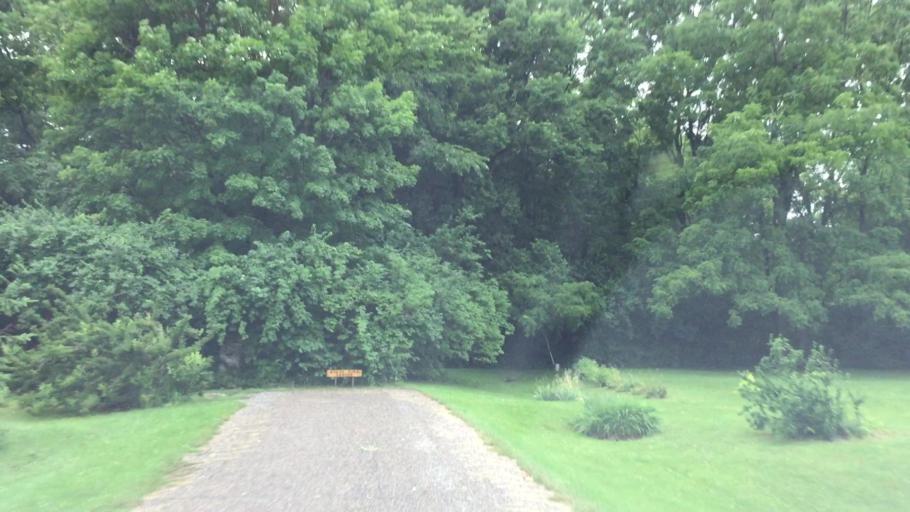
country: US
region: Illinois
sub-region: Hancock County
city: Nauvoo
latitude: 40.5326
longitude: -91.3729
